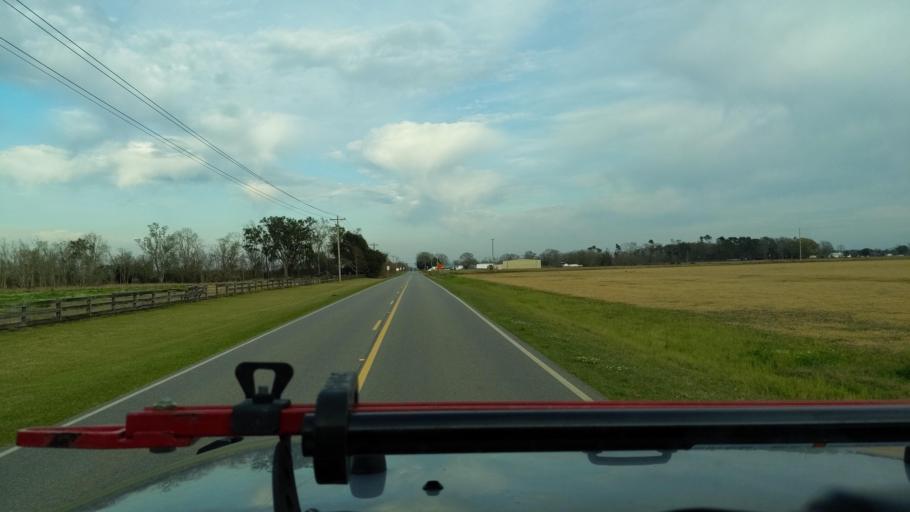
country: US
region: Alabama
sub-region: Baldwin County
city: Foley
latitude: 30.4580
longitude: -87.7194
